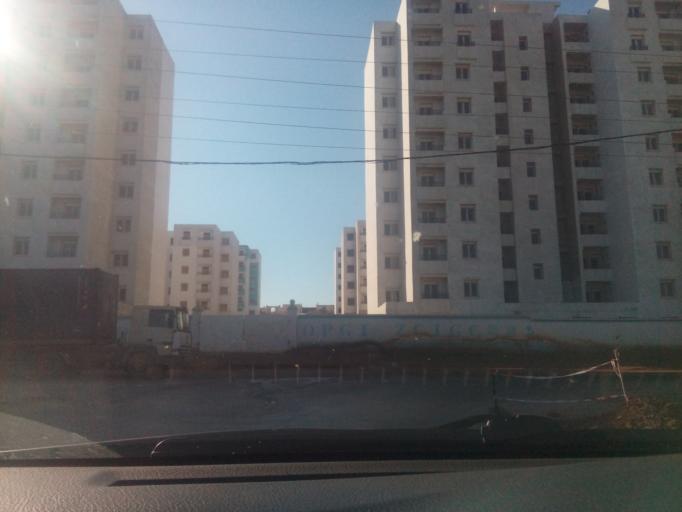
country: DZ
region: Oran
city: Es Senia
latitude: 35.6785
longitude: -0.6035
